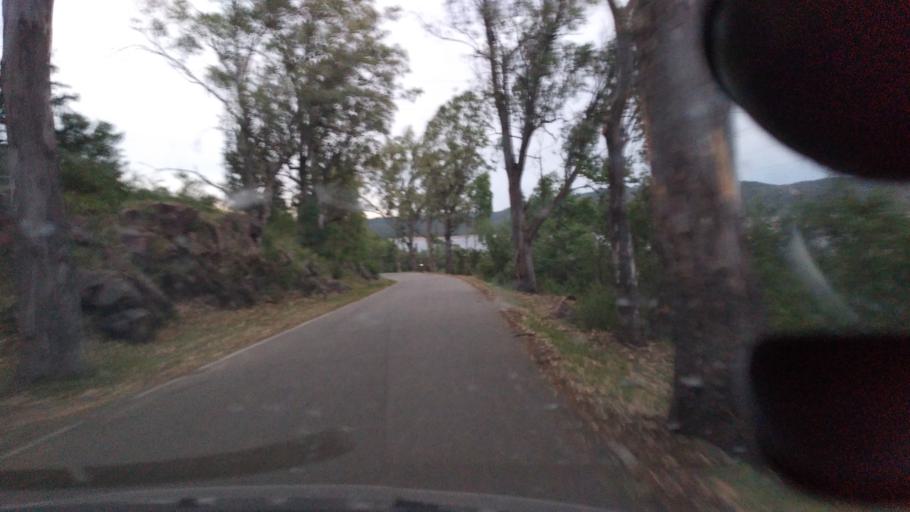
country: AR
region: Cordoba
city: Villa Las Rosas
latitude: -31.8753
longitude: -65.0301
